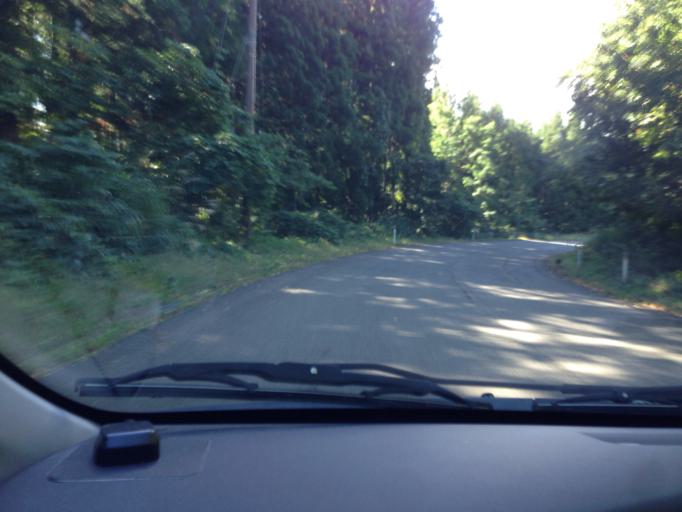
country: JP
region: Fukushima
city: Inawashiro
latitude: 37.5810
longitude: 140.1095
